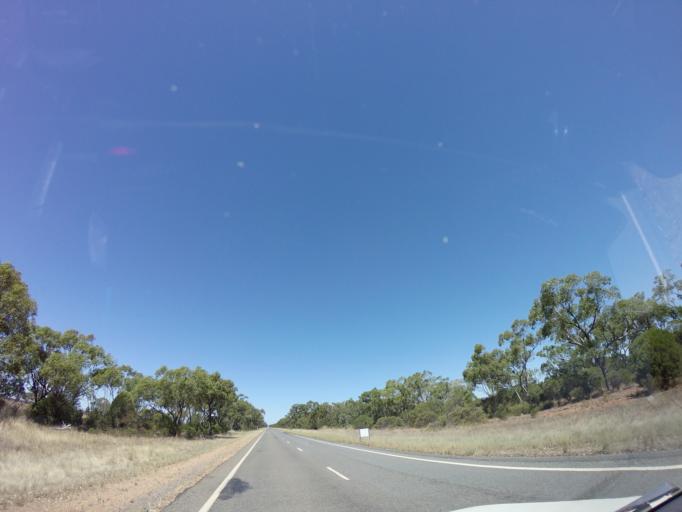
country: AU
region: New South Wales
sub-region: Bogan
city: Nyngan
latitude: -31.5455
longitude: 146.7398
